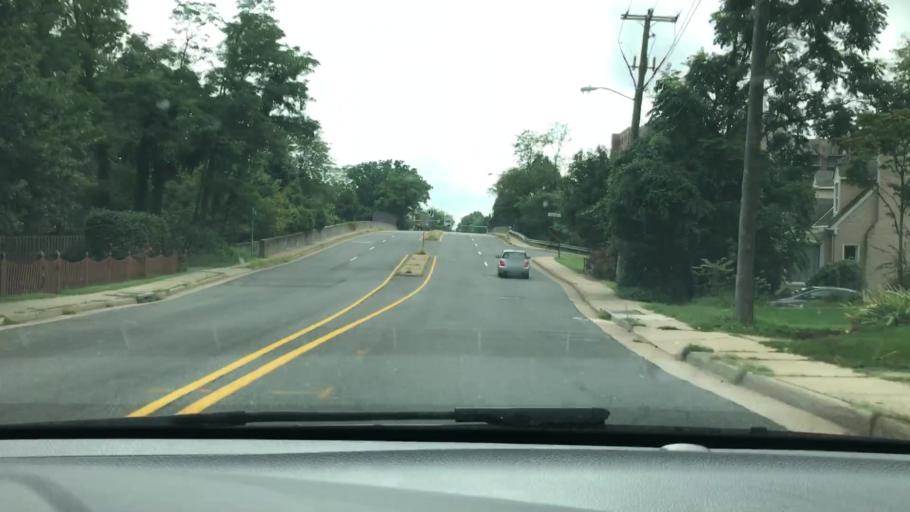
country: US
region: Virginia
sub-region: Arlington County
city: Arlington
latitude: 38.8853
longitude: -77.1205
